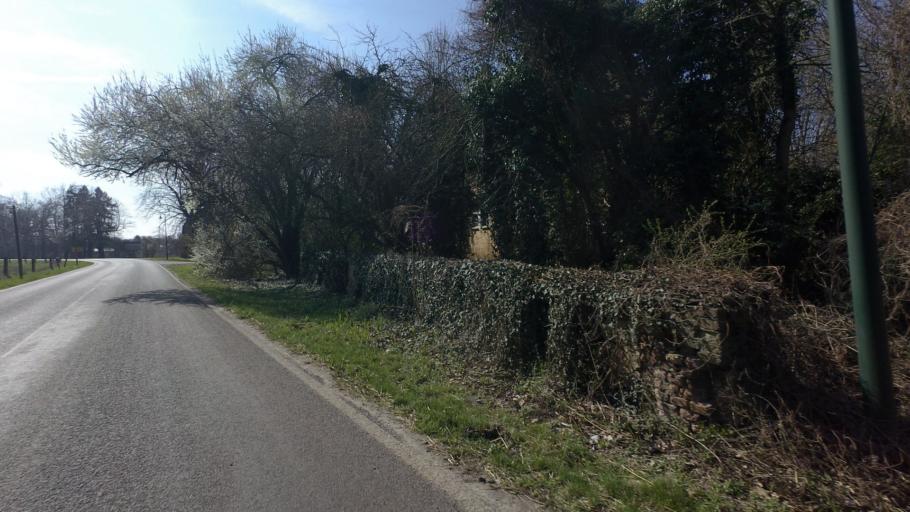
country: DE
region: Brandenburg
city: Sperenberg
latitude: 52.0510
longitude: 13.3206
